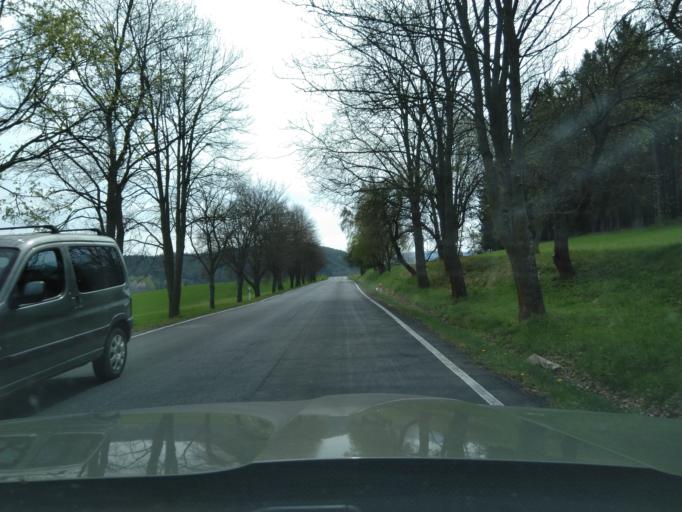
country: CZ
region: Plzensky
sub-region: Okres Klatovy
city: Susice
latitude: 49.2453
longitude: 13.5736
